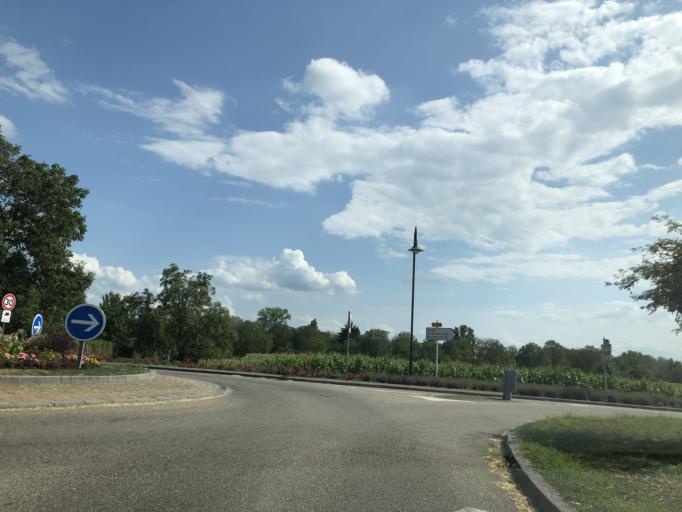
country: FR
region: Alsace
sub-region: Departement du Bas-Rhin
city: Valff
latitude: 48.4222
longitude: 7.5114
